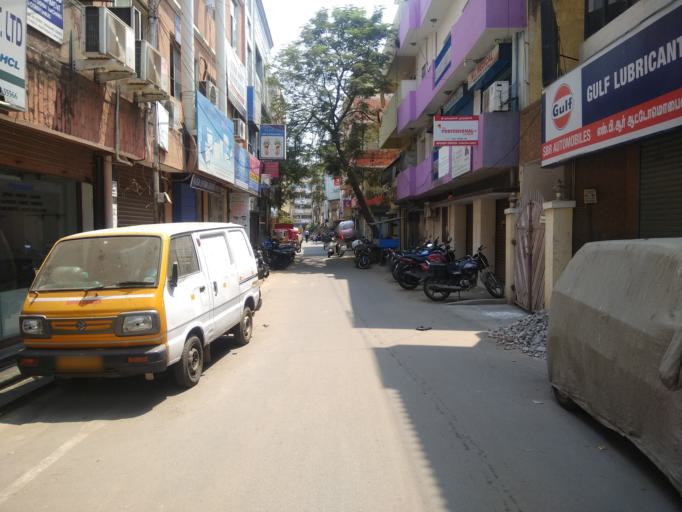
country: IN
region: Tamil Nadu
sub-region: Chennai
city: Chetput
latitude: 13.0553
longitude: 80.2540
